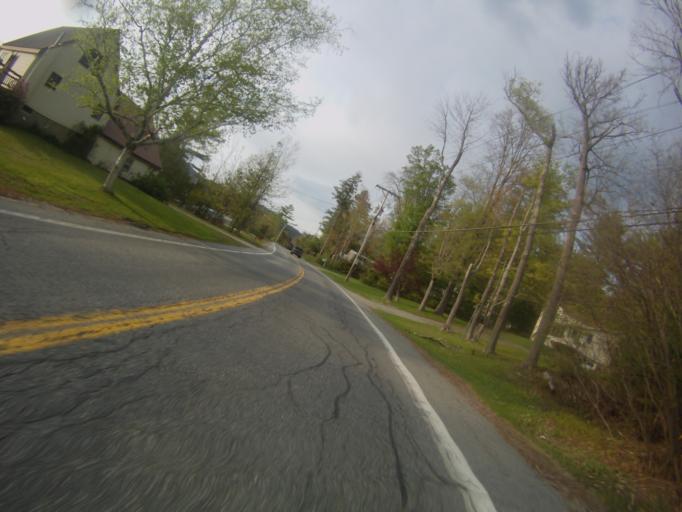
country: US
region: New York
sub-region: Warren County
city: Warrensburg
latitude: 43.6940
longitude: -73.7195
